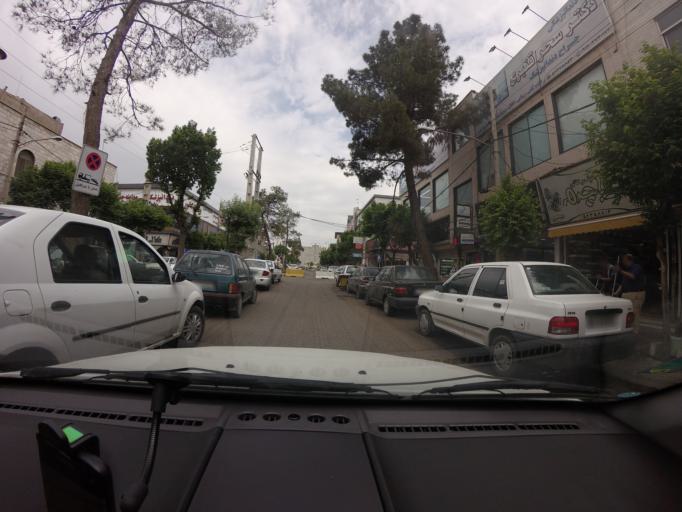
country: IR
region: Tehran
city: Eslamshahr
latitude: 35.5571
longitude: 51.2468
